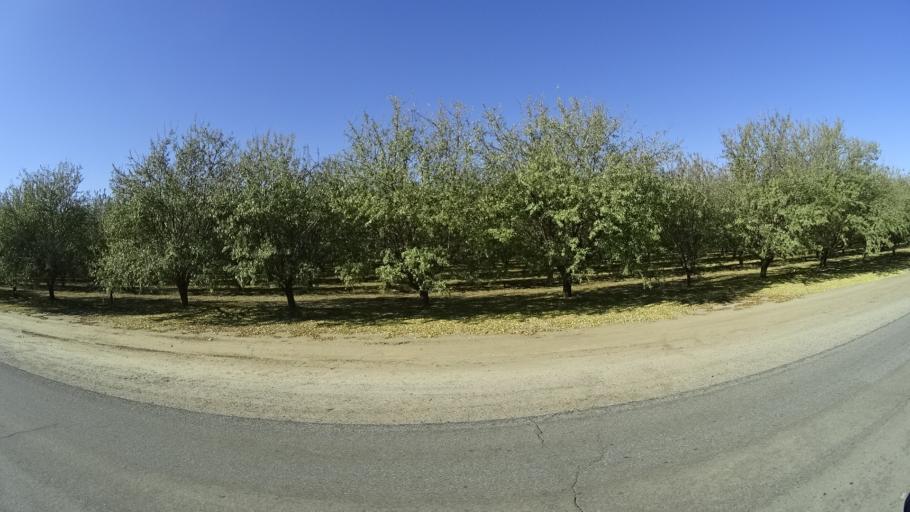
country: US
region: California
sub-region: Kern County
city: Greenfield
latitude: 35.2509
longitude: -119.0567
